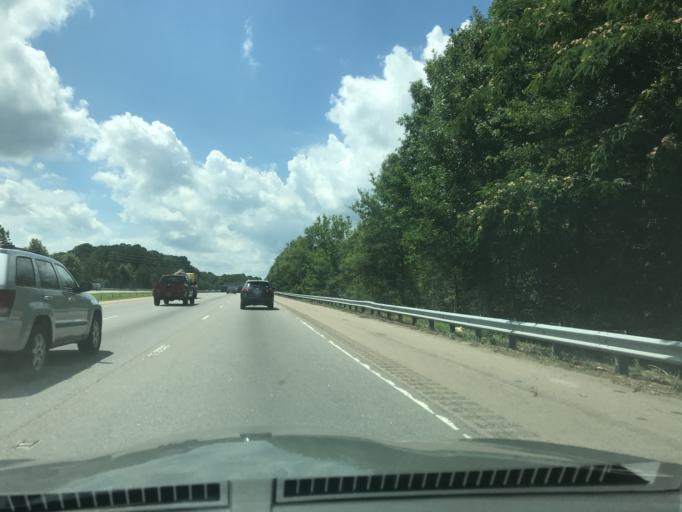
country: US
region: North Carolina
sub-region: Wake County
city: Wake Forest
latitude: 35.8929
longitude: -78.5978
